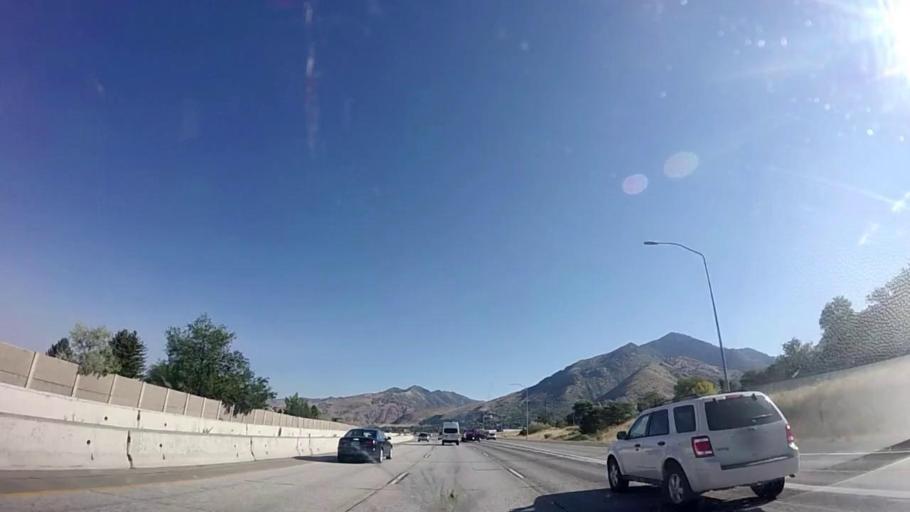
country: US
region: Utah
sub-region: Salt Lake County
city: Mount Olympus
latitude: 40.6806
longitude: -111.7982
